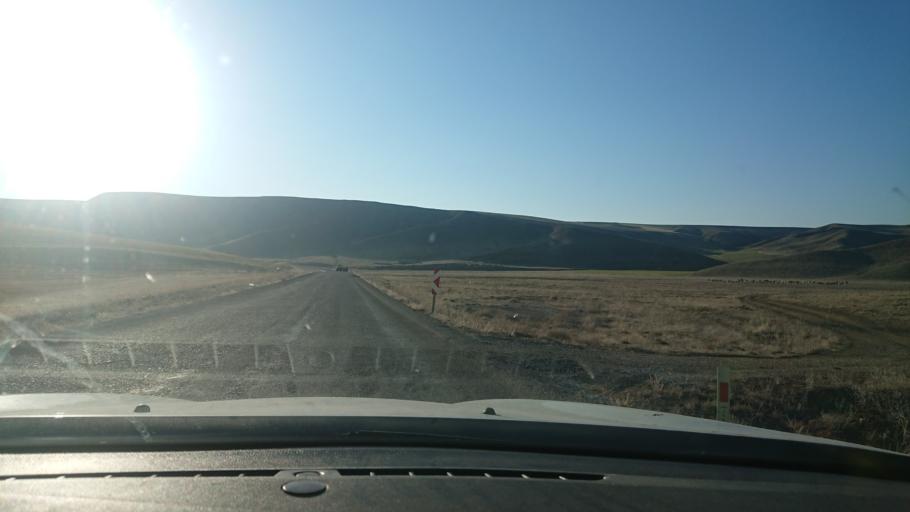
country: TR
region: Aksaray
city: Acipinar
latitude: 38.7115
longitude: 33.7650
